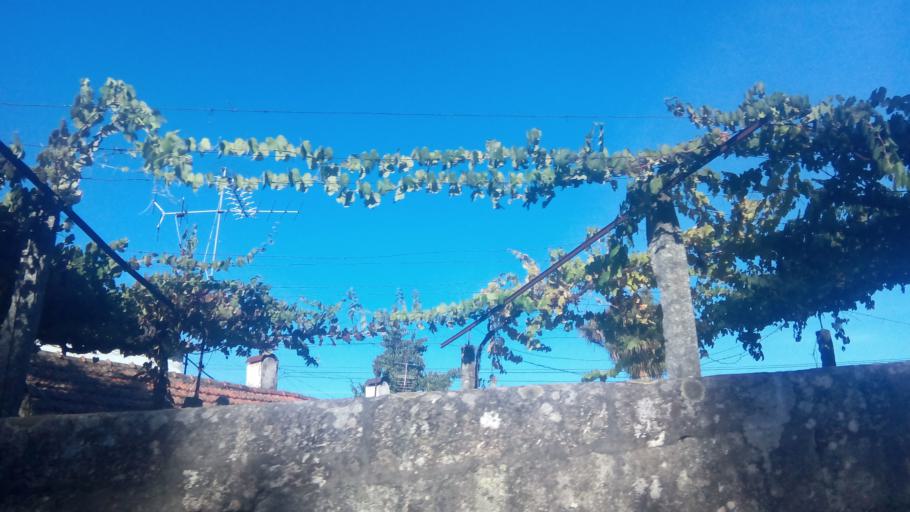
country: PT
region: Porto
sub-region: Paredes
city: Casteloes de Cepeda
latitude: 41.1976
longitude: -8.3461
